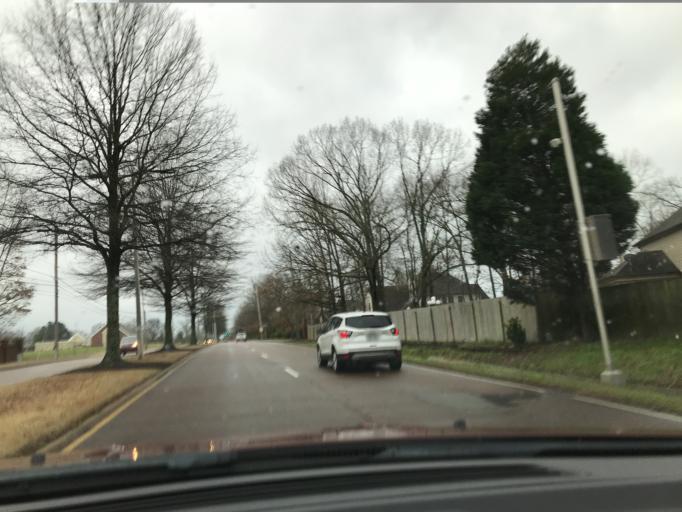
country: US
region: Tennessee
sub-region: Shelby County
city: Collierville
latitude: 35.0581
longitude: -89.6861
